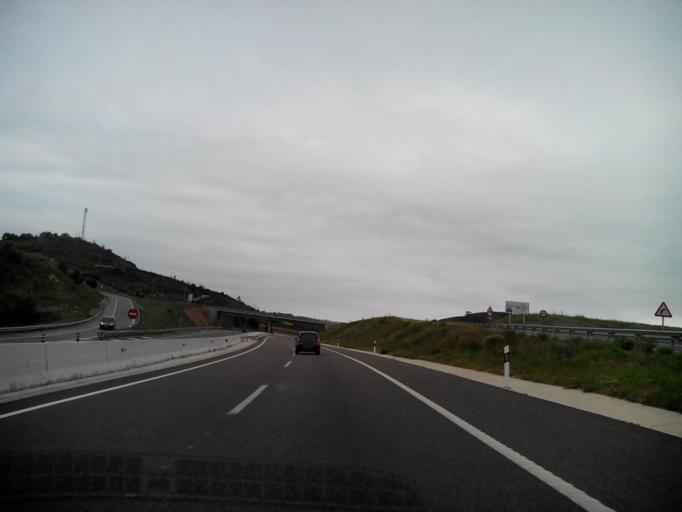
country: ES
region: Catalonia
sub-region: Provincia de Barcelona
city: Calaf
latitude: 41.7378
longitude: 1.5042
